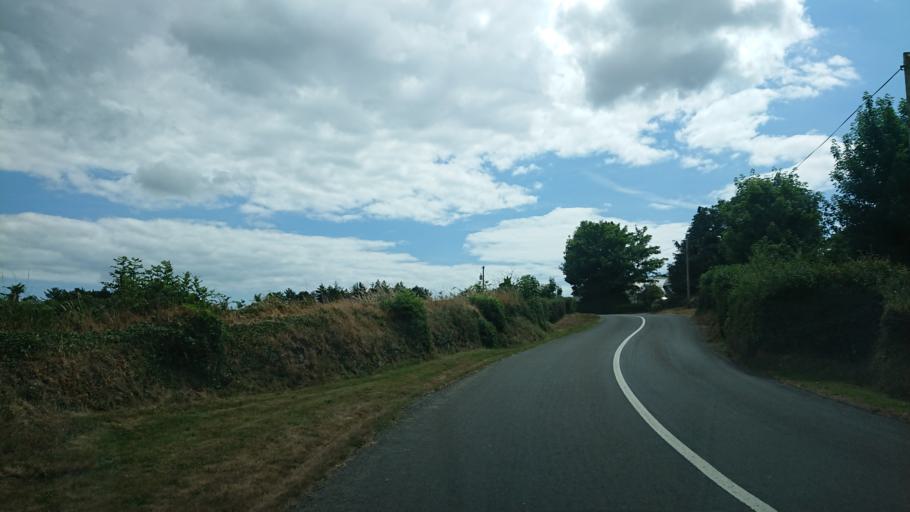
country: IE
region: Munster
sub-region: Waterford
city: Portlaw
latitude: 52.2240
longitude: -7.3362
